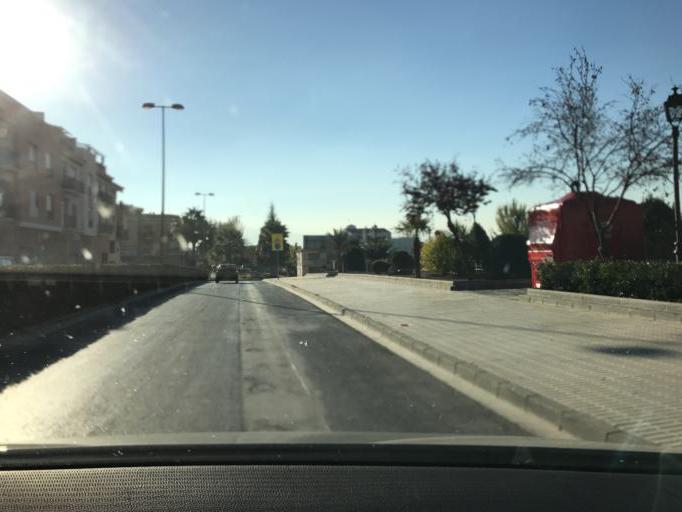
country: ES
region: Andalusia
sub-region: Provincia de Granada
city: Peligros
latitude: 37.2349
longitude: -3.6317
